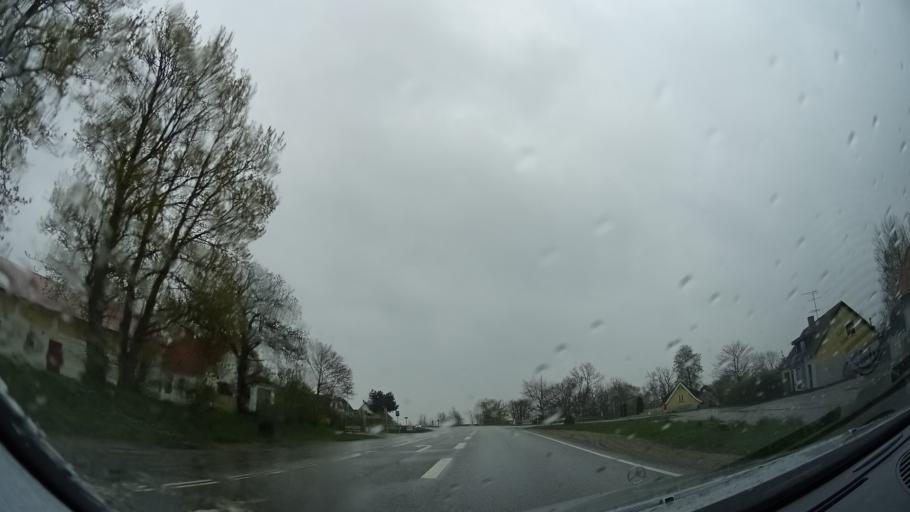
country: DK
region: Zealand
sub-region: Odsherred Kommune
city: Asnaes
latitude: 55.8053
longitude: 11.5969
